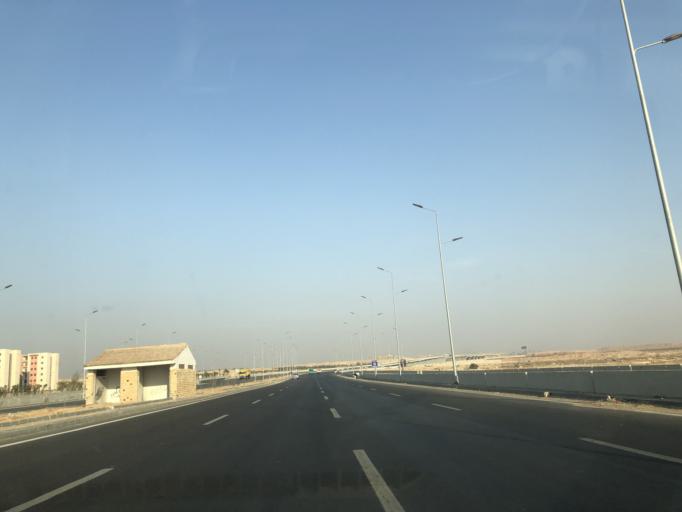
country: EG
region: Al Jizah
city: Madinat Sittah Uktubar
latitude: 29.9051
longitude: 30.9752
